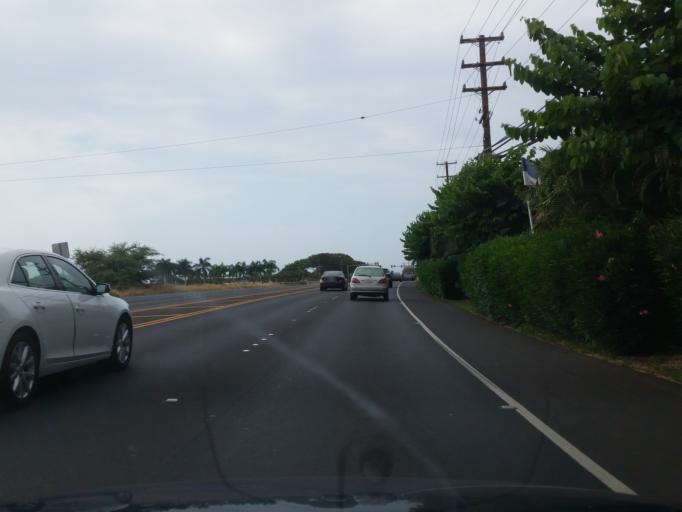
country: US
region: Hawaii
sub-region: Maui County
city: Lahaina
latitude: 20.8827
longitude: -156.6816
